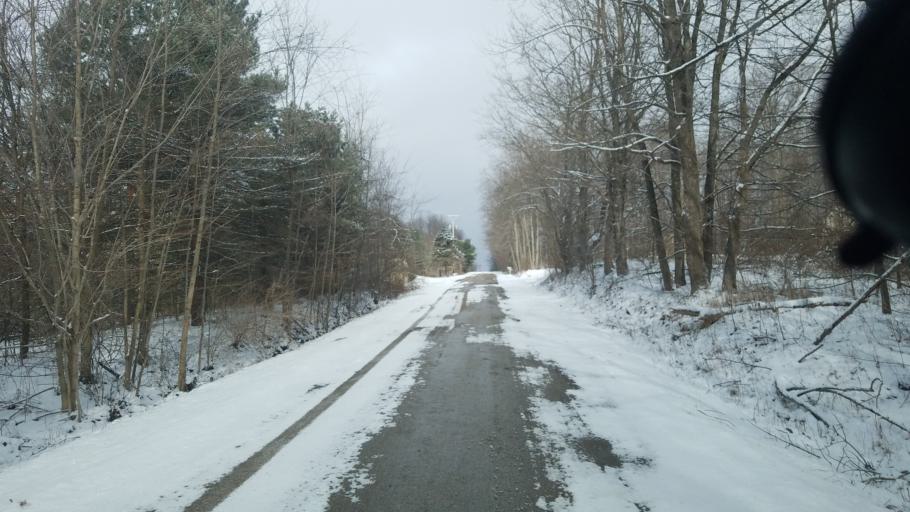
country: US
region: Ohio
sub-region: Richland County
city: Lexington
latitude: 40.6675
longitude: -82.6450
